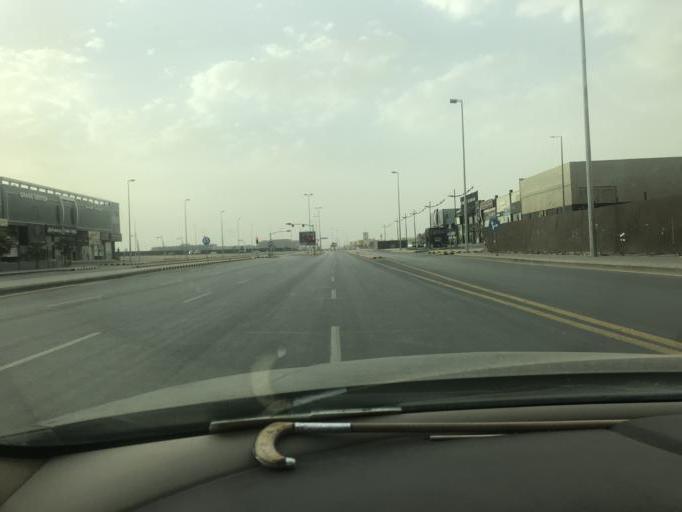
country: SA
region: Ar Riyad
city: Riyadh
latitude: 24.7970
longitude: 46.6549
